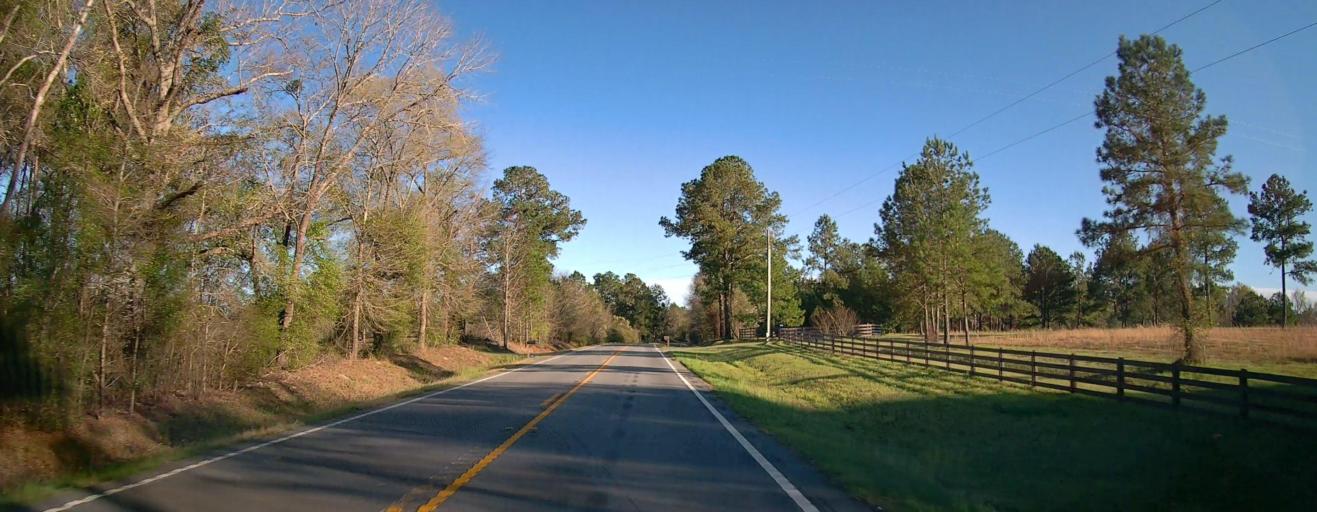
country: US
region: Georgia
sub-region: Pulaski County
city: Hawkinsville
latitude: 32.2372
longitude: -83.4005
